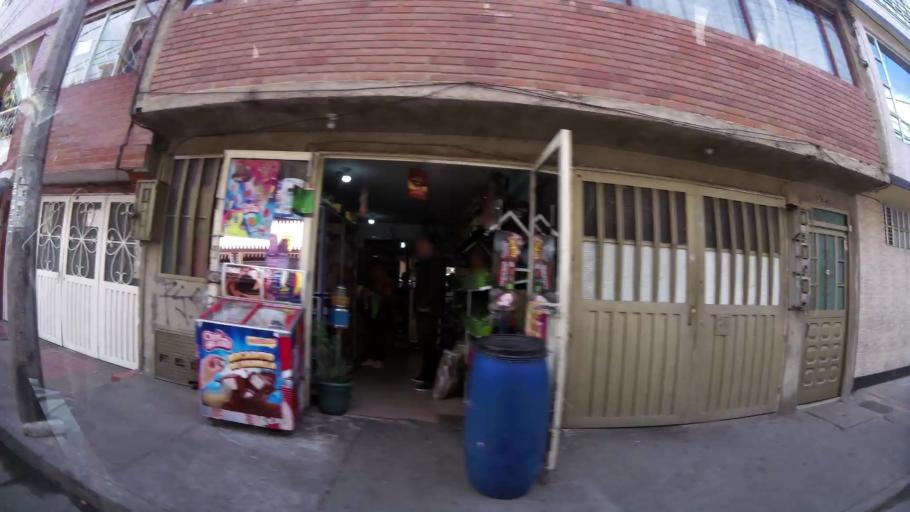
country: CO
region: Bogota D.C.
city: Bogota
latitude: 4.6195
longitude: -74.1289
